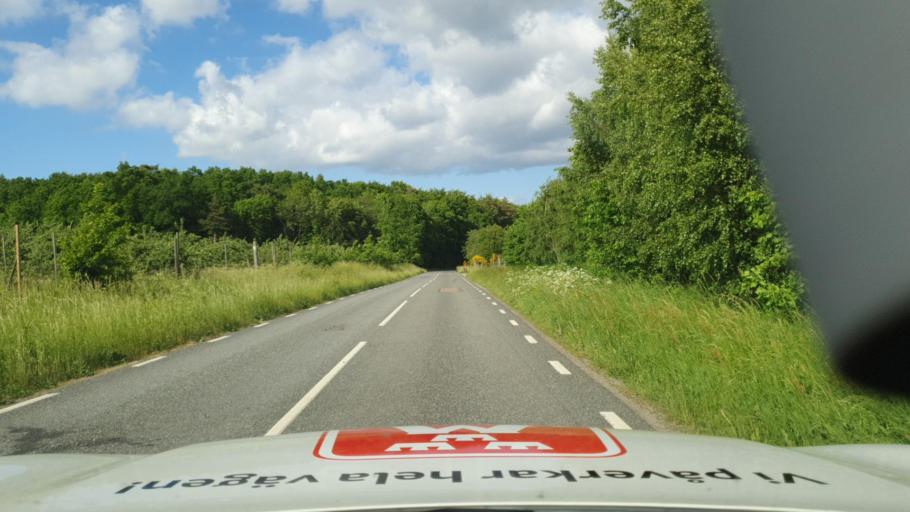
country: SE
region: Skane
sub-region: Simrishamns Kommun
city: Kivik
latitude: 55.6144
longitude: 14.2274
